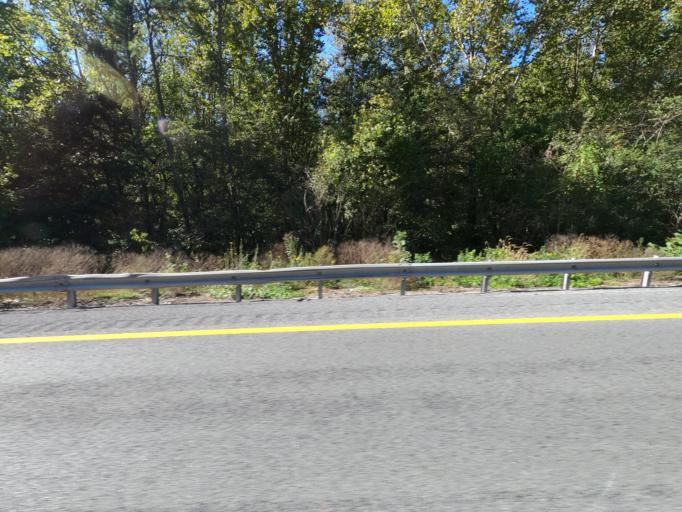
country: US
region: Tennessee
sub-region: Cheatham County
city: Pegram
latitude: 36.0846
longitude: -87.0461
